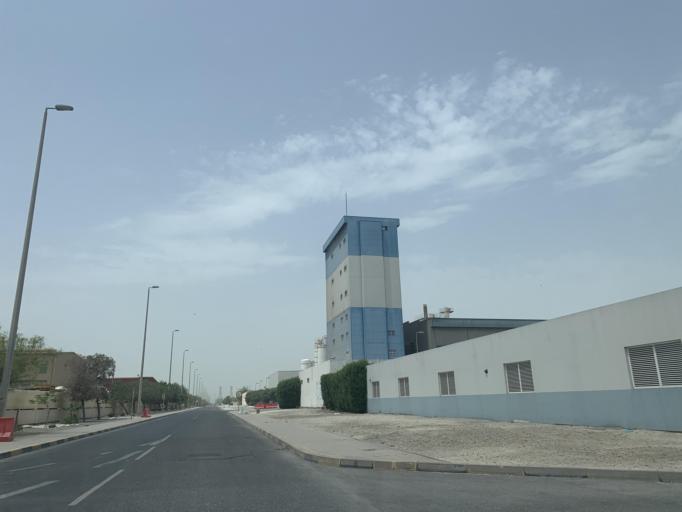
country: BH
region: Muharraq
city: Al Hadd
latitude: 26.2163
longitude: 50.6787
